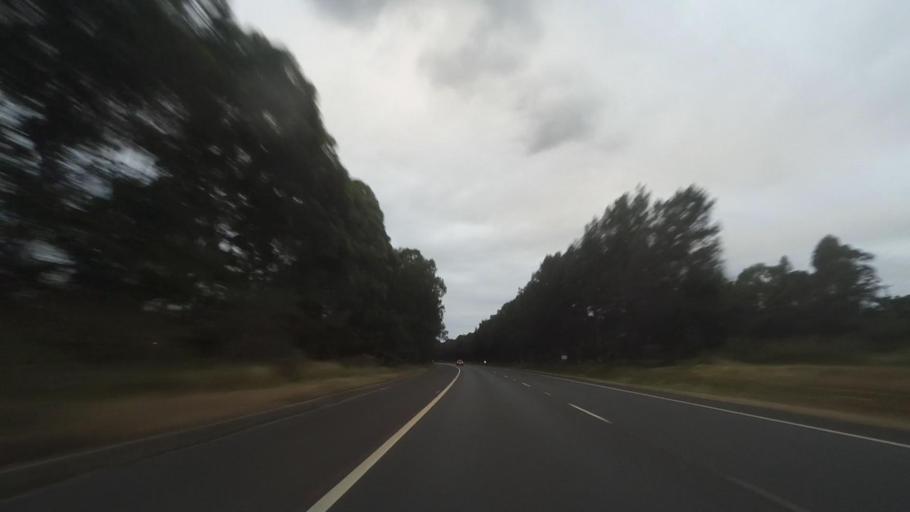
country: AU
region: New South Wales
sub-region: Wollongong
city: Berkeley
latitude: -34.4643
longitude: 150.8489
